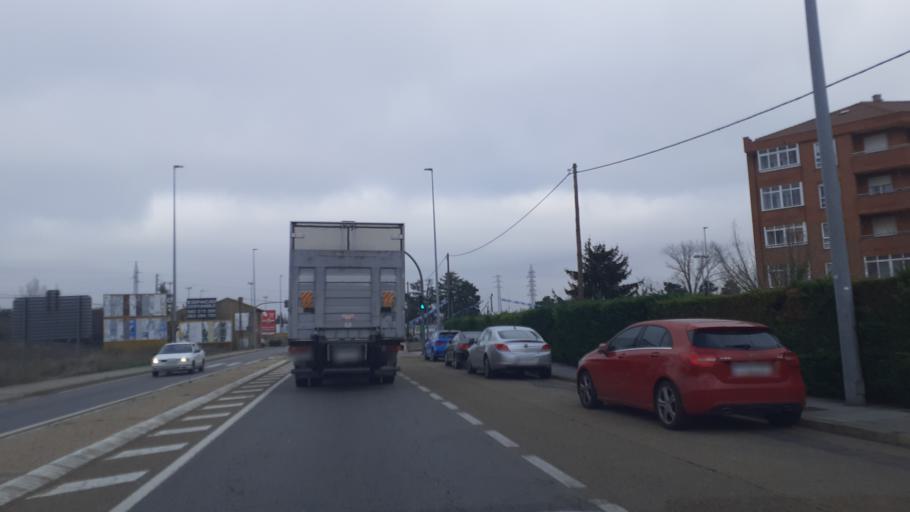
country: ES
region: Castille and Leon
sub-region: Provincia de Leon
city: Leon
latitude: 42.5657
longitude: -5.5822
